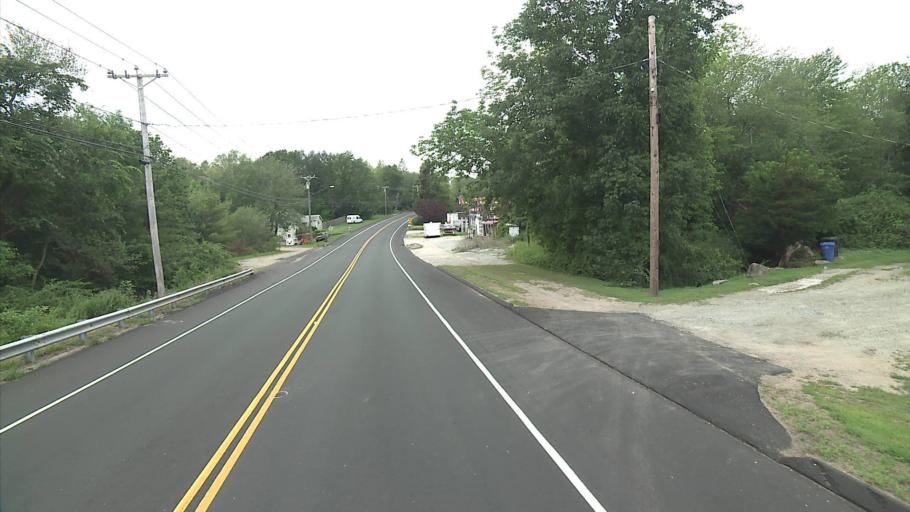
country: US
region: Connecticut
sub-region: New London County
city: Preston City
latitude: 41.5730
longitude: -71.8765
